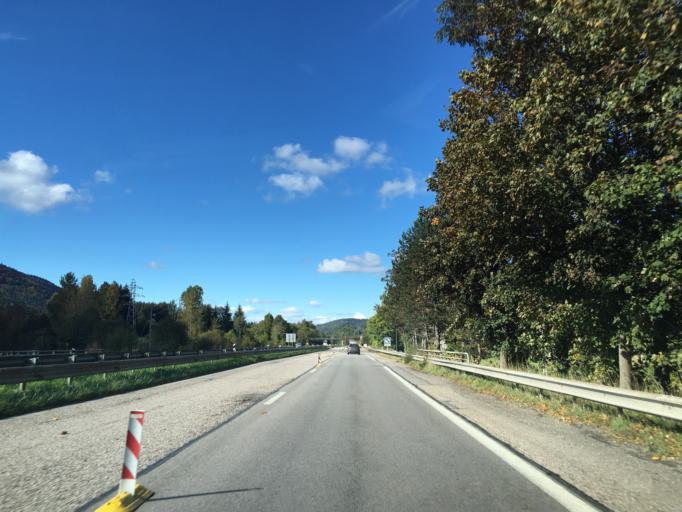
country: FR
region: Lorraine
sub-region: Departement des Vosges
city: Etival-Clairefontaine
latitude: 48.3811
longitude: 6.8712
